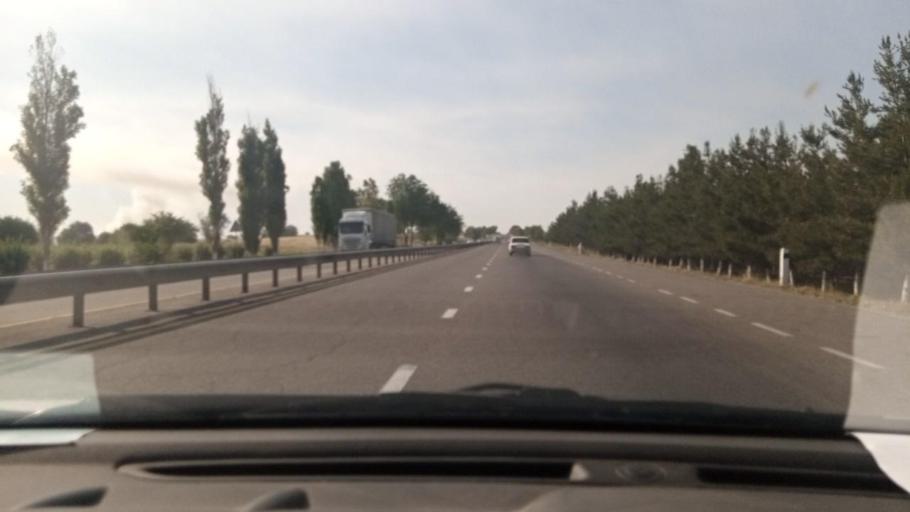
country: UZ
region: Toshkent
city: Tuytepa
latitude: 41.1171
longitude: 69.4441
